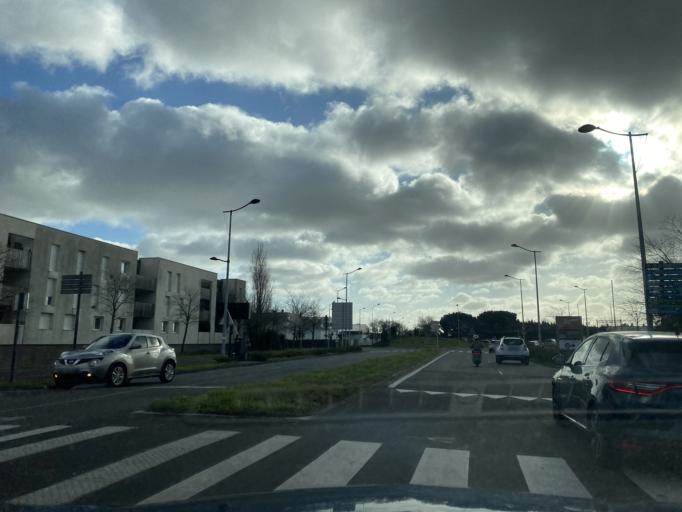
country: FR
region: Aquitaine
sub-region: Departement de la Gironde
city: Le Haillan
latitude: 44.8423
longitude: -0.6704
